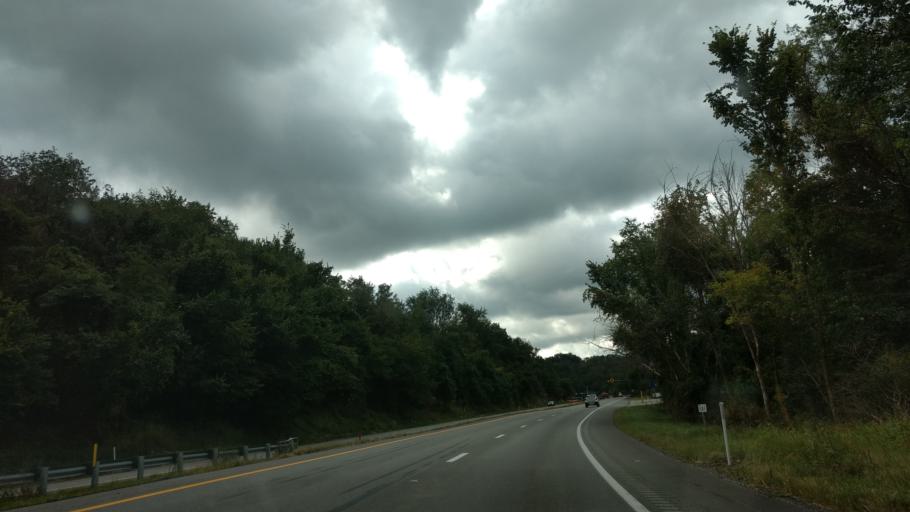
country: US
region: Pennsylvania
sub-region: Westmoreland County
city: Fellsburg
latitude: 40.1910
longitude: -79.8209
